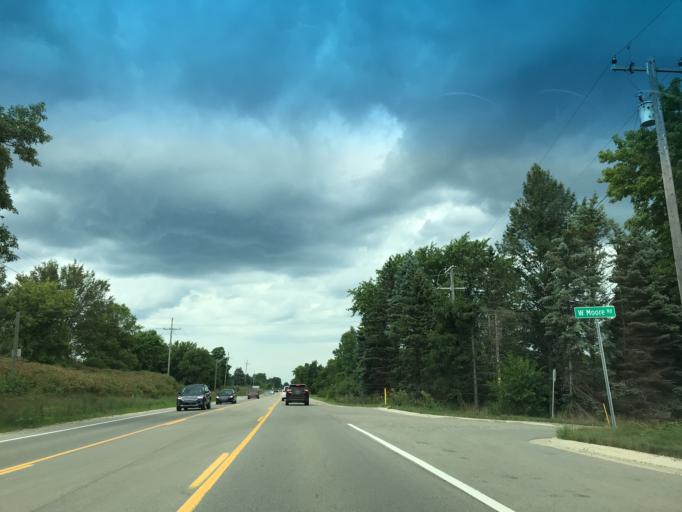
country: US
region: Michigan
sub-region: Oakland County
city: Milford
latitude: 42.5285
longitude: -83.6163
